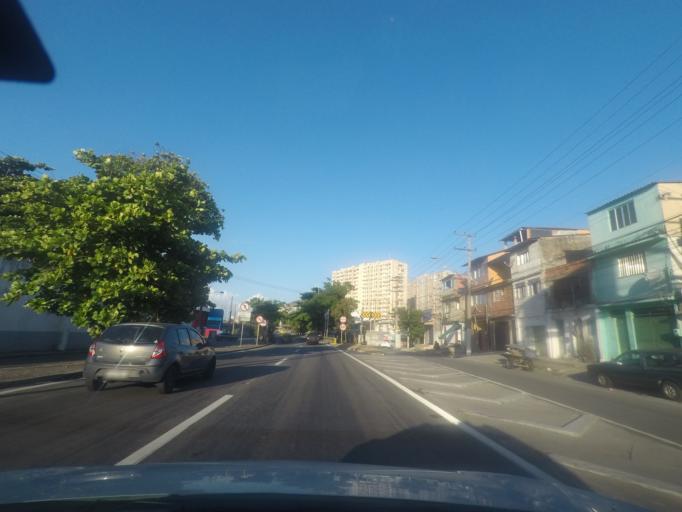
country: BR
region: Rio de Janeiro
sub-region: Niteroi
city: Niteroi
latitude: -22.8854
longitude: -43.1141
